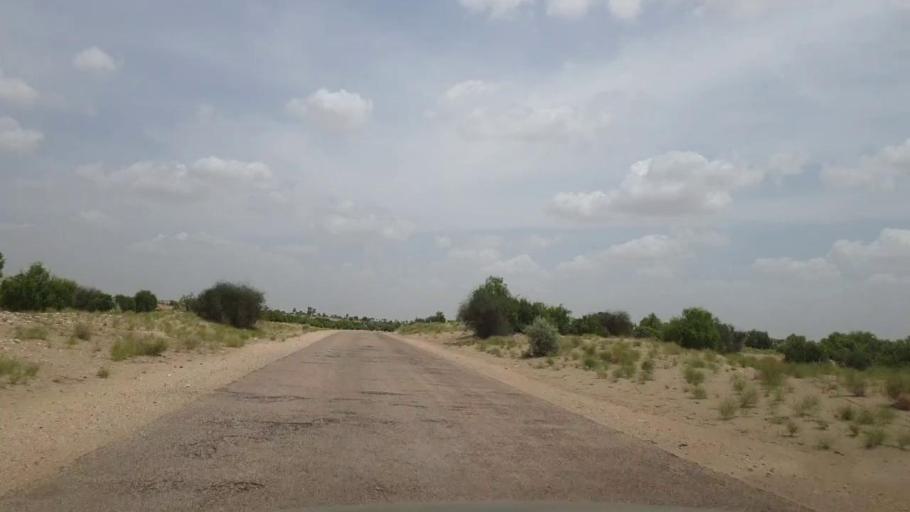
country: PK
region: Sindh
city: Kot Diji
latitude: 27.1915
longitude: 69.1668
